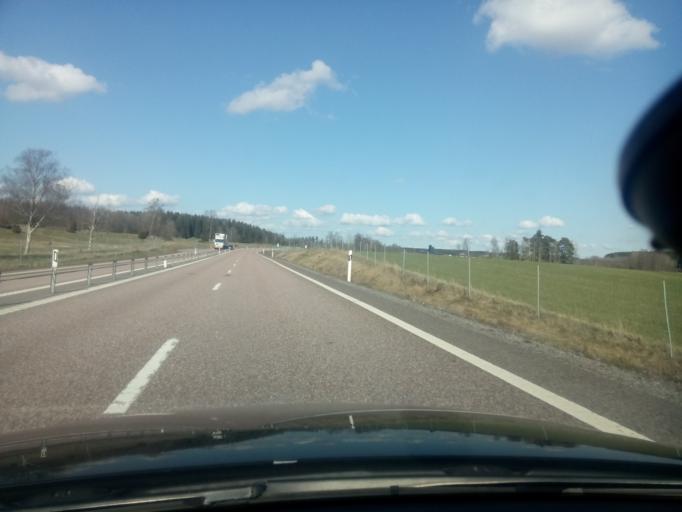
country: SE
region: Soedermanland
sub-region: Flens Kommun
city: Malmkoping
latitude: 59.1587
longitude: 16.7422
